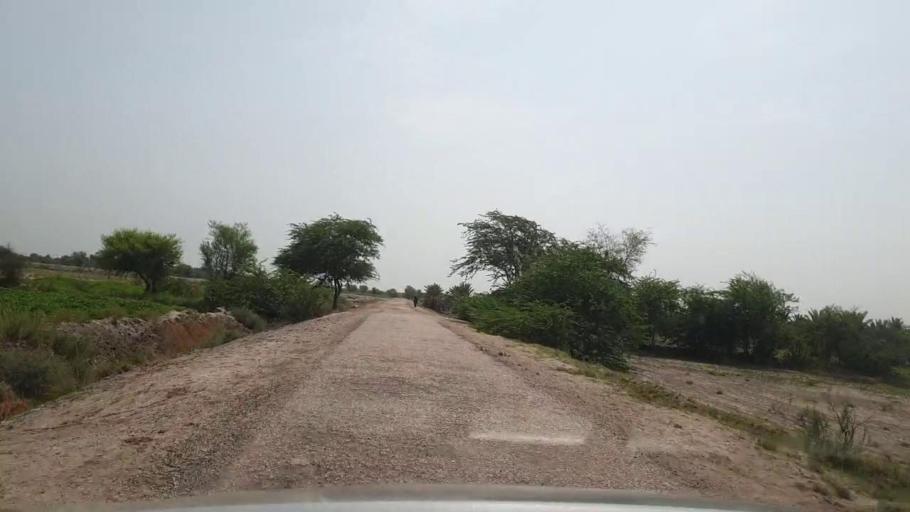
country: PK
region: Sindh
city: Pano Aqil
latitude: 27.6169
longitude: 69.1392
